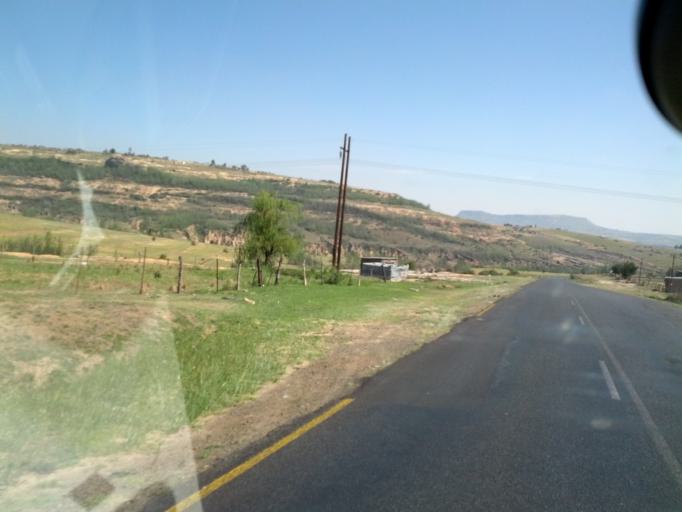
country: LS
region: Berea
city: Teyateyaneng
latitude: -29.1442
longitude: 27.7045
